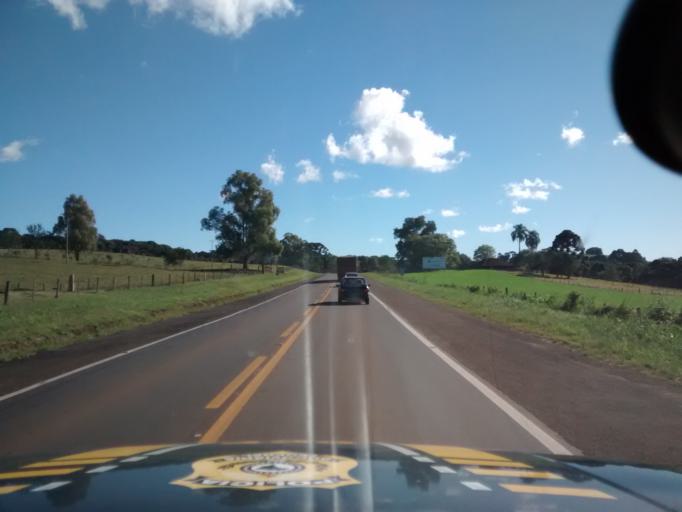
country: BR
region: Rio Grande do Sul
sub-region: Lagoa Vermelha
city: Lagoa Vermelha
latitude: -28.2937
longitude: -51.4417
